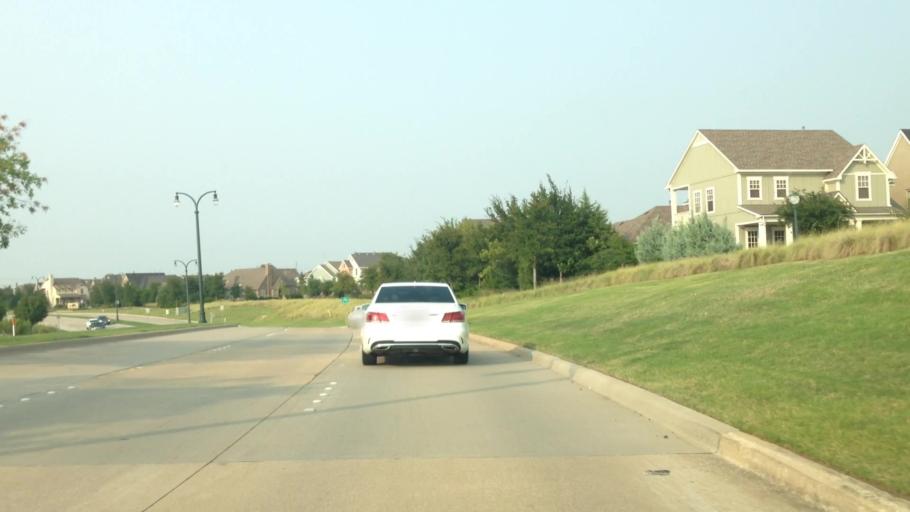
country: US
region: Texas
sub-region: Denton County
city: The Colony
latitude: 33.0503
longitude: -96.8666
